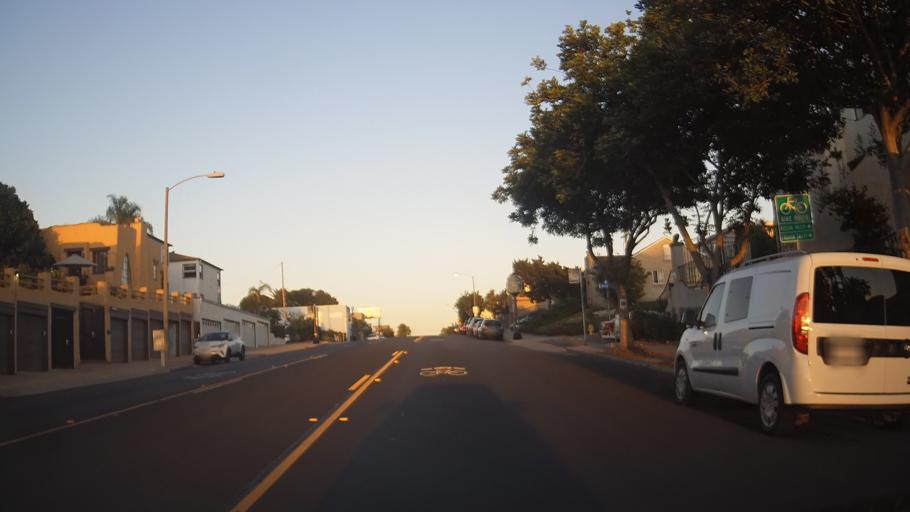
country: US
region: California
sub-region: San Diego County
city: San Diego
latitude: 32.7628
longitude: -117.1381
